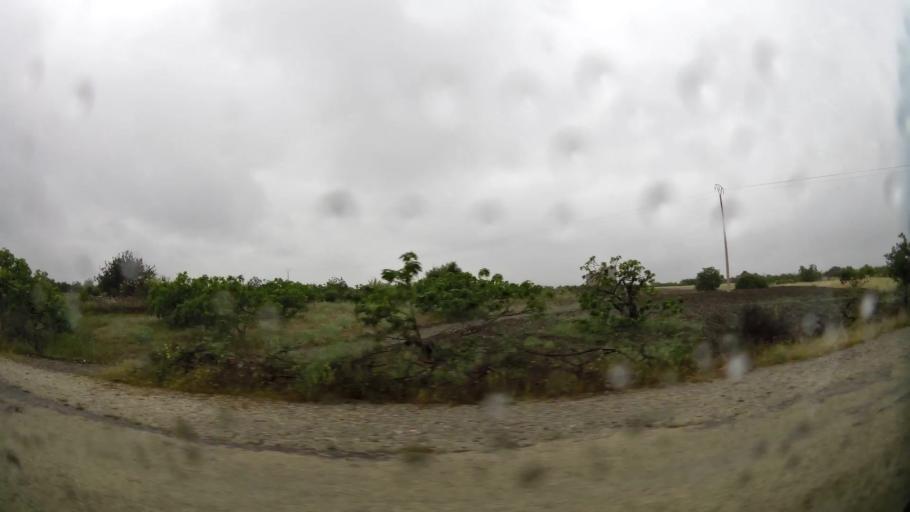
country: MA
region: Taza-Al Hoceima-Taounate
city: Imzourene
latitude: 35.1340
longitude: -3.7820
